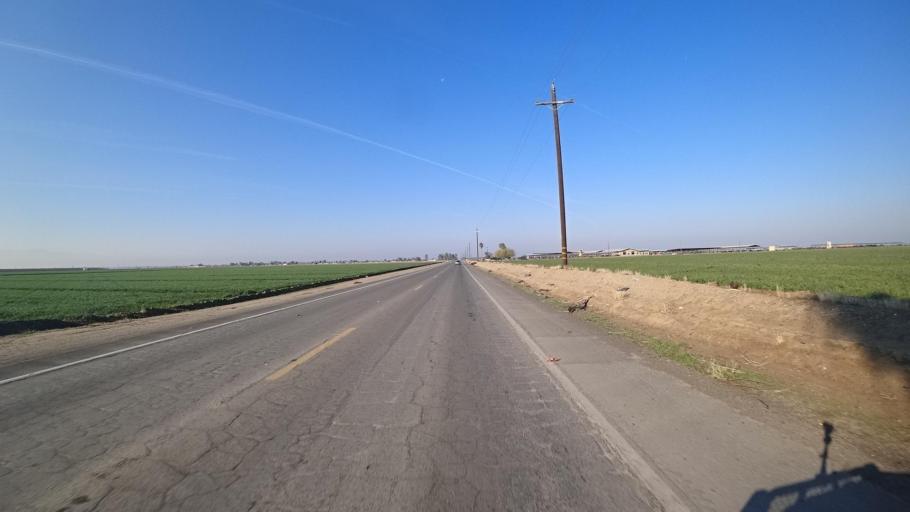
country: US
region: California
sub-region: Kern County
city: Lamont
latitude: 35.2524
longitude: -118.9420
